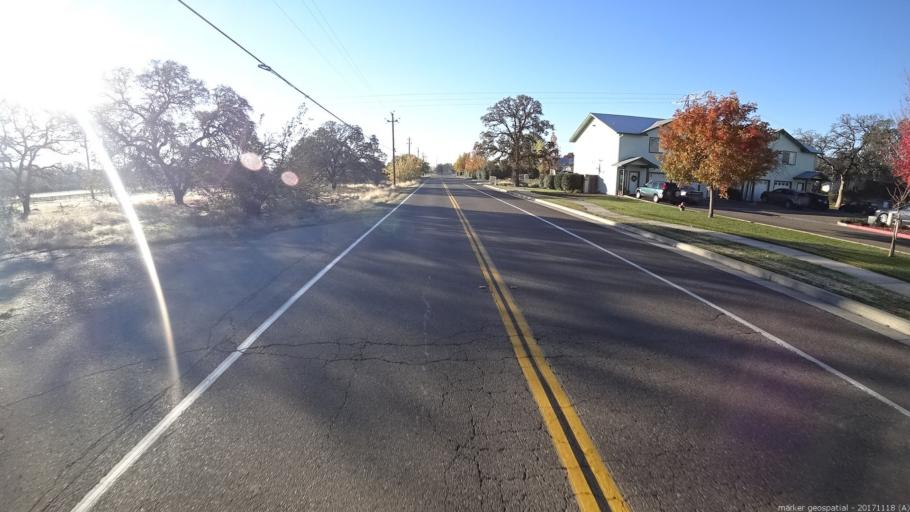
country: US
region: California
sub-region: Shasta County
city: Cottonwood
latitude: 40.3999
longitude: -122.2840
